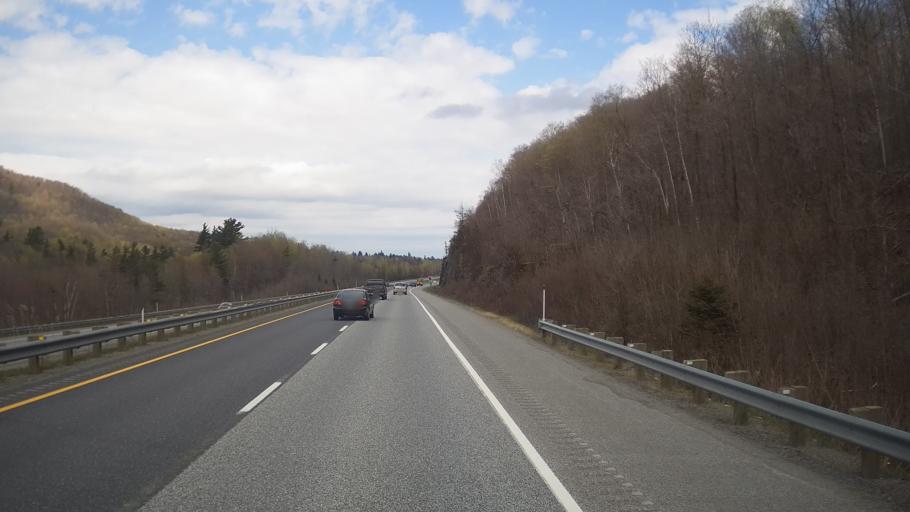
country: CA
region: Quebec
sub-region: Estrie
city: Magog
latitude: 45.2906
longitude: -72.2410
